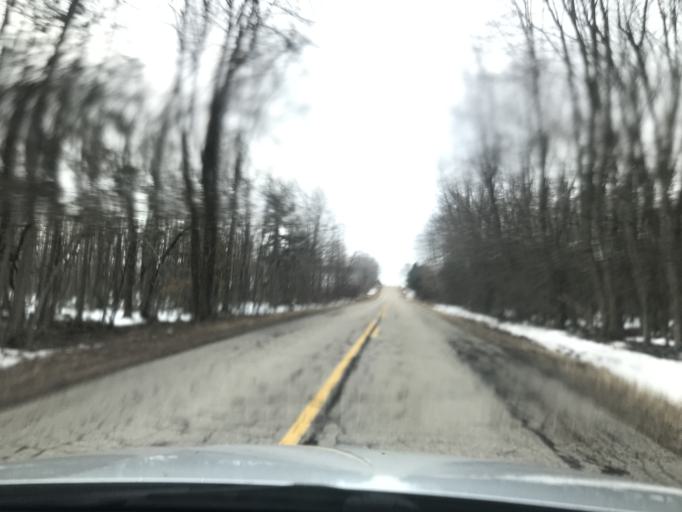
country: US
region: Wisconsin
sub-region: Oconto County
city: Oconto Falls
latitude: 44.8343
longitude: -88.1680
